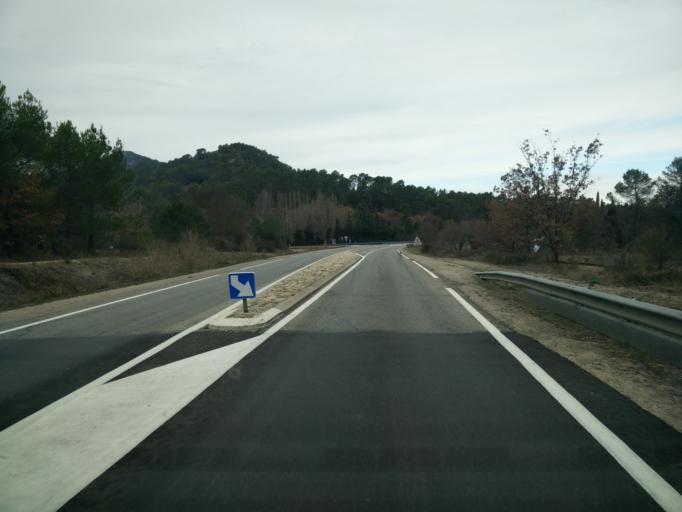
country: FR
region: Provence-Alpes-Cote d'Azur
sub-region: Departement du Var
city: La Celle
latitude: 43.3849
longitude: 6.0485
